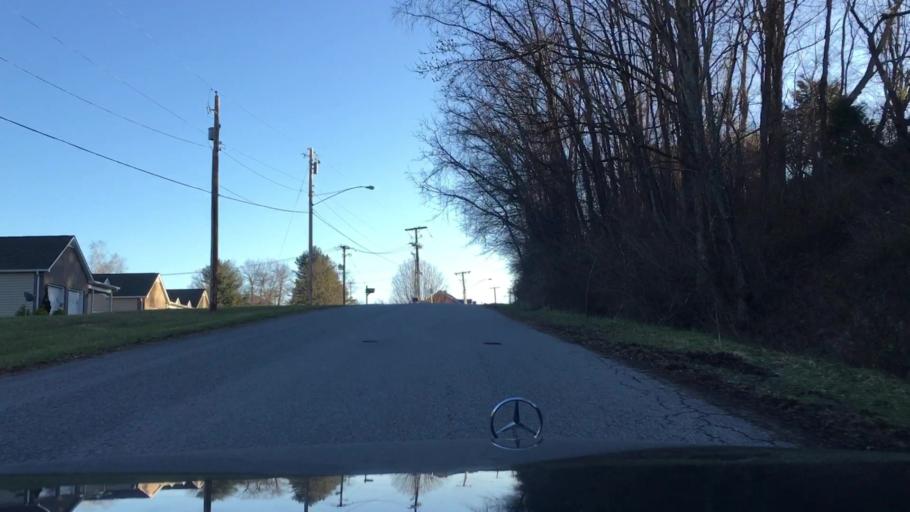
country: US
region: Virginia
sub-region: Montgomery County
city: Merrimac
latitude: 37.1658
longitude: -80.4436
